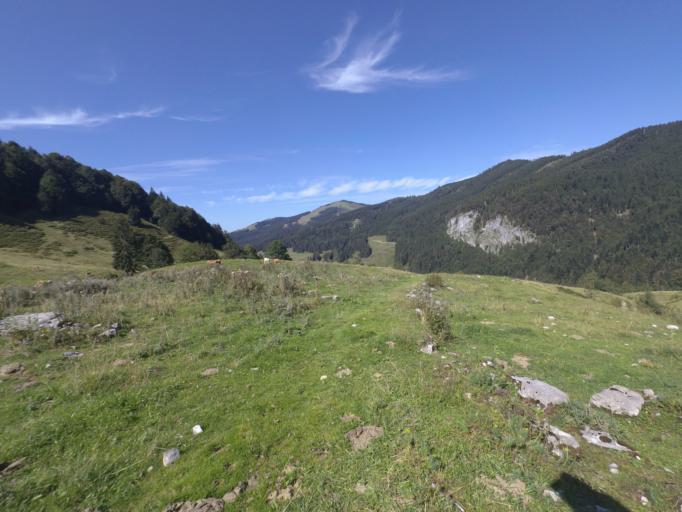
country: AT
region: Salzburg
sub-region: Politischer Bezirk Salzburg-Umgebung
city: Hintersee
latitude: 47.6908
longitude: 13.2420
